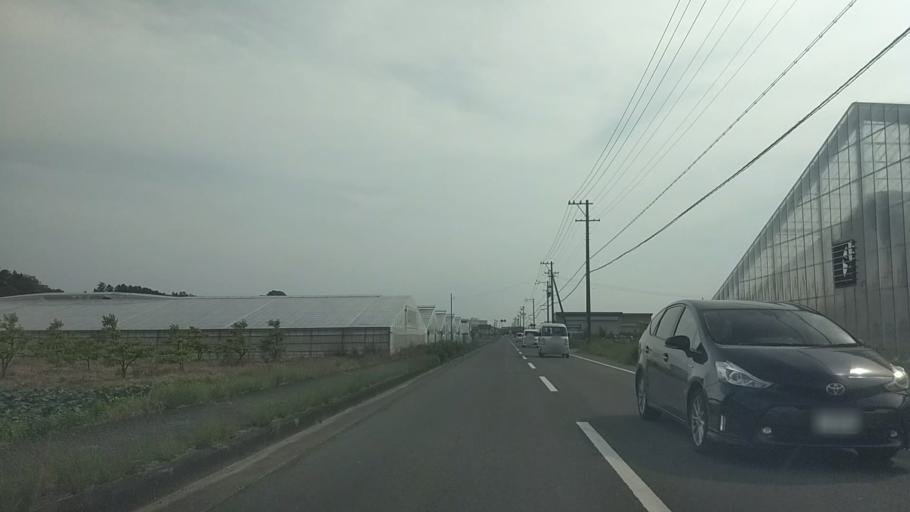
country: JP
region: Shizuoka
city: Kosai-shi
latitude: 34.7224
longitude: 137.6286
